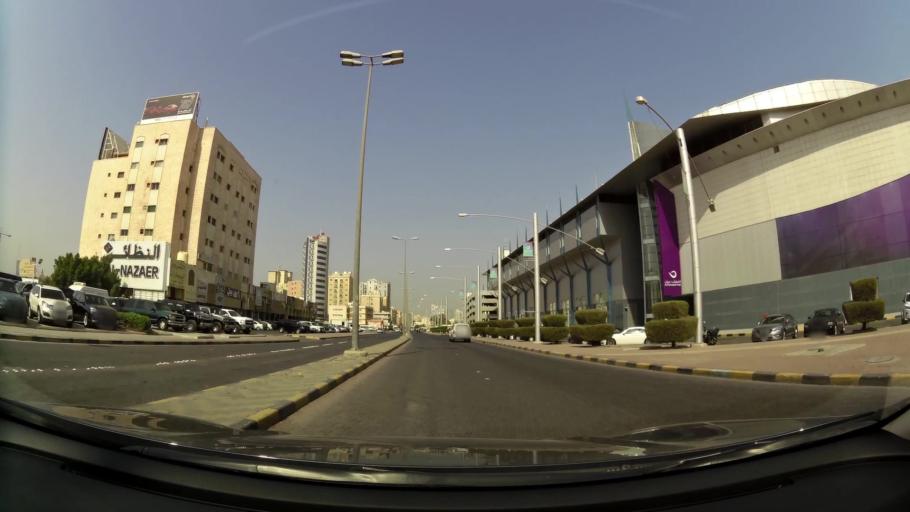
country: KW
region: Muhafazat Hawalli
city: Hawalli
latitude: 29.3400
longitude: 48.0262
